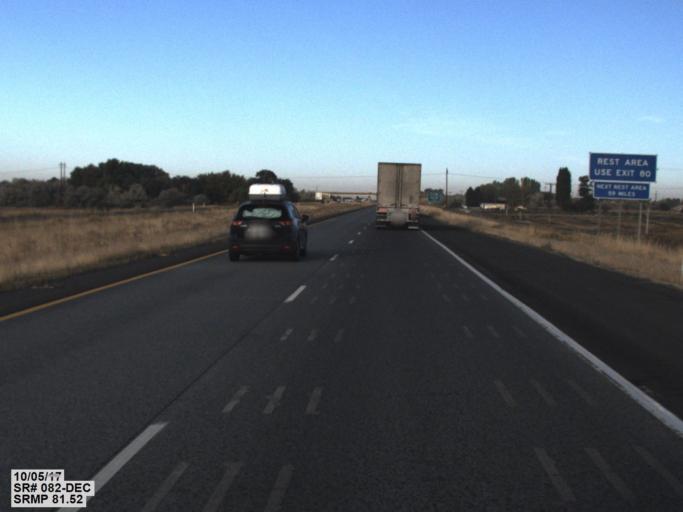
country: US
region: Washington
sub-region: Benton County
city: Prosser
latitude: 46.2214
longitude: -119.7575
